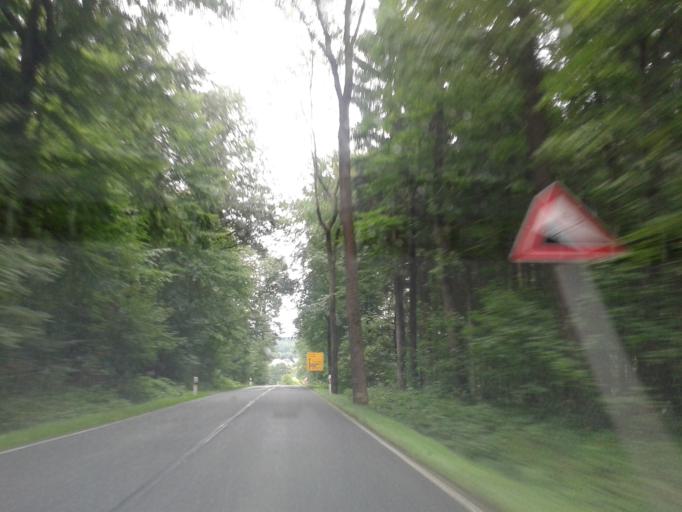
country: DE
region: Saxony
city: Obercunnersdorf
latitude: 50.9507
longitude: 13.4965
